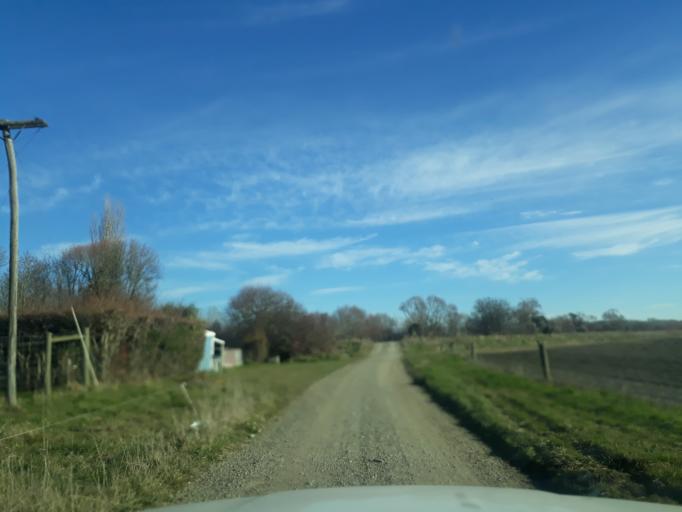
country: NZ
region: Canterbury
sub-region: Timaru District
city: Timaru
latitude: -44.2696
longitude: 171.3335
